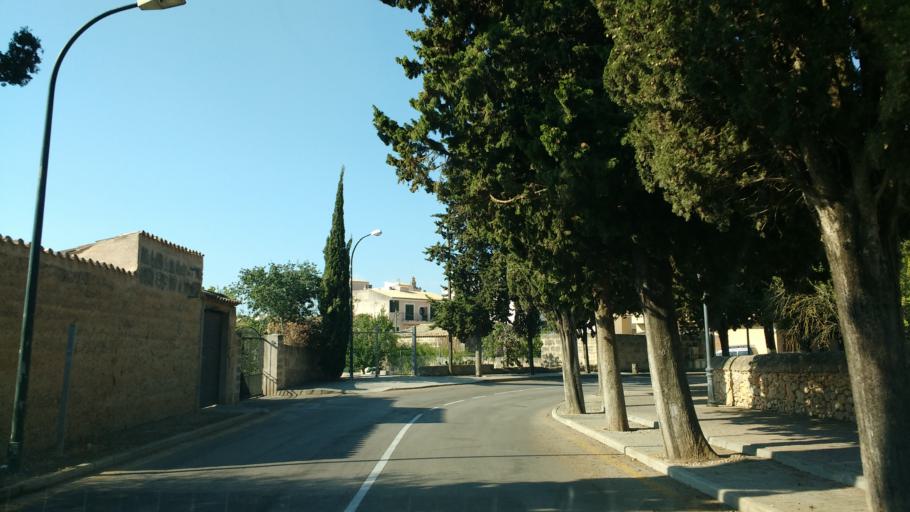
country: ES
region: Balearic Islands
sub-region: Illes Balears
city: Consell
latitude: 39.6712
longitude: 2.8144
